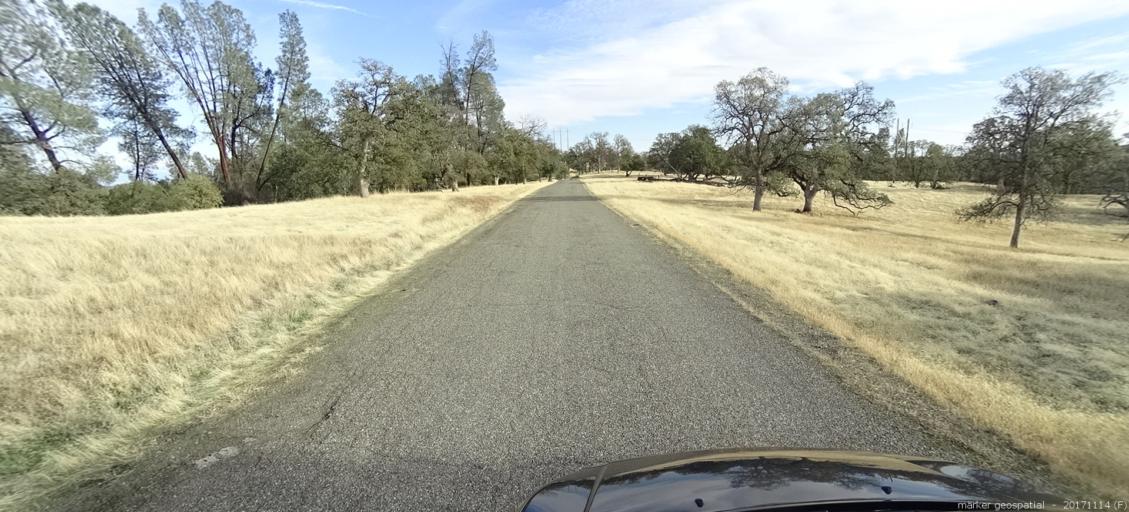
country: US
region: California
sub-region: Shasta County
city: Shasta
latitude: 40.3832
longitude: -122.5829
